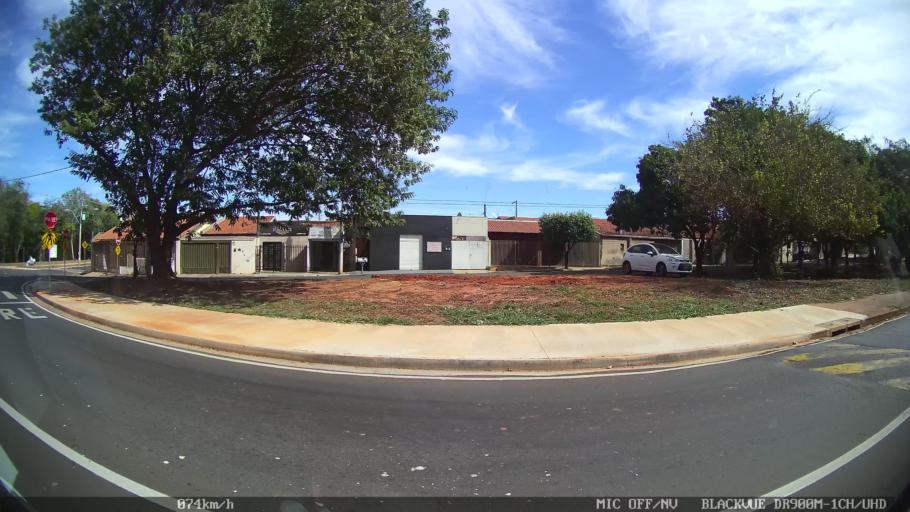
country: BR
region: Sao Paulo
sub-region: Sao Jose Do Rio Preto
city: Sao Jose do Rio Preto
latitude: -20.8367
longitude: -49.3456
